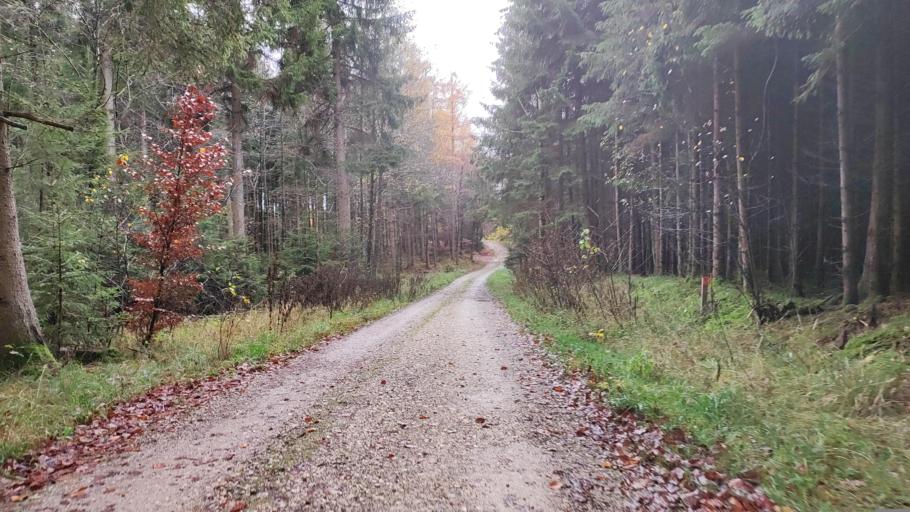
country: DE
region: Bavaria
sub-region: Swabia
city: Burtenbach
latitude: 48.3618
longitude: 10.5169
